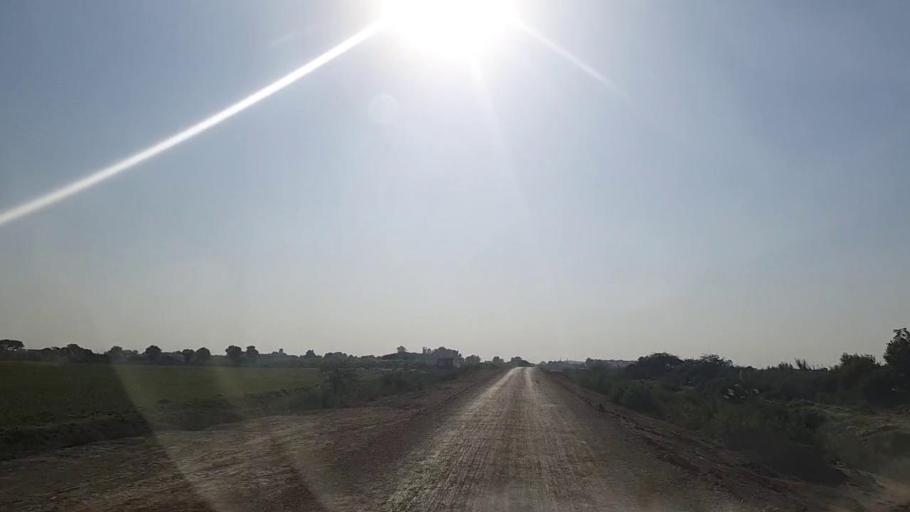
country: PK
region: Sindh
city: Mirpur Batoro
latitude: 24.5449
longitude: 68.1530
